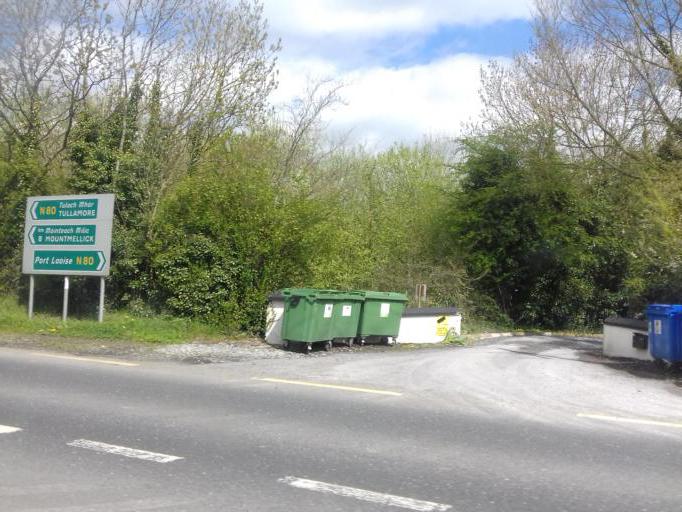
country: IE
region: Leinster
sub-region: Laois
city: Portlaoise
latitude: 53.0547
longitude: -7.3225
